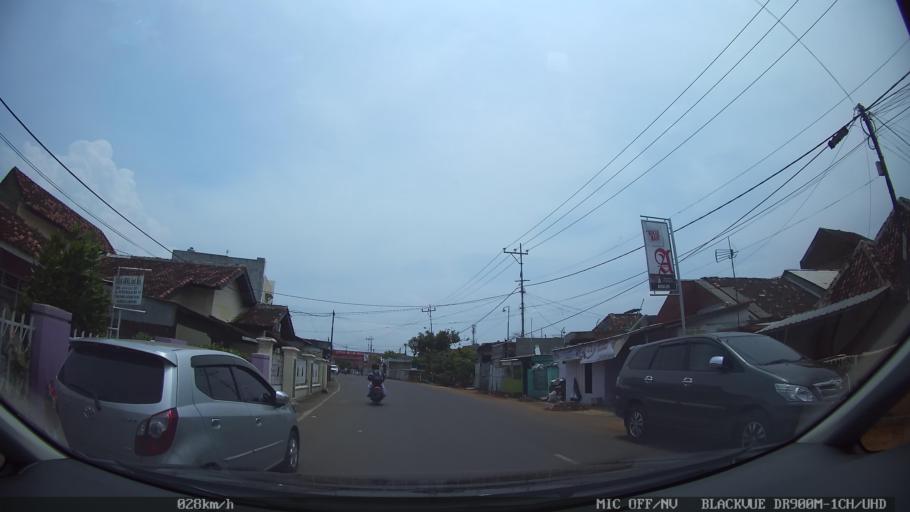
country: ID
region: Lampung
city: Bandarlampung
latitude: -5.4104
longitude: 105.2696
